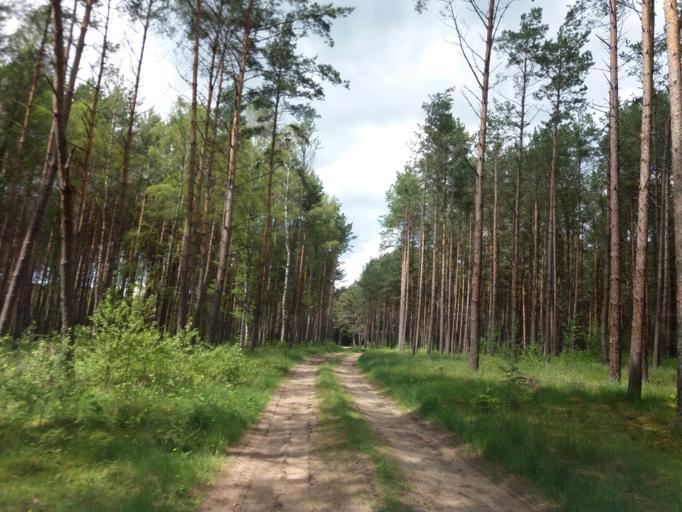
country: PL
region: West Pomeranian Voivodeship
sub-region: Powiat choszczenski
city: Drawno
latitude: 53.2800
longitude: 15.7294
